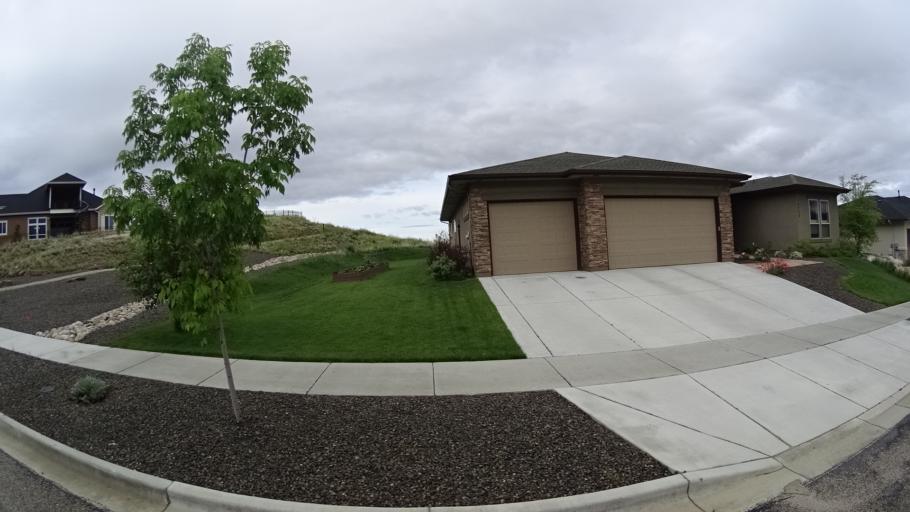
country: US
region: Idaho
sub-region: Ada County
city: Eagle
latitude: 43.7706
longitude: -116.2546
